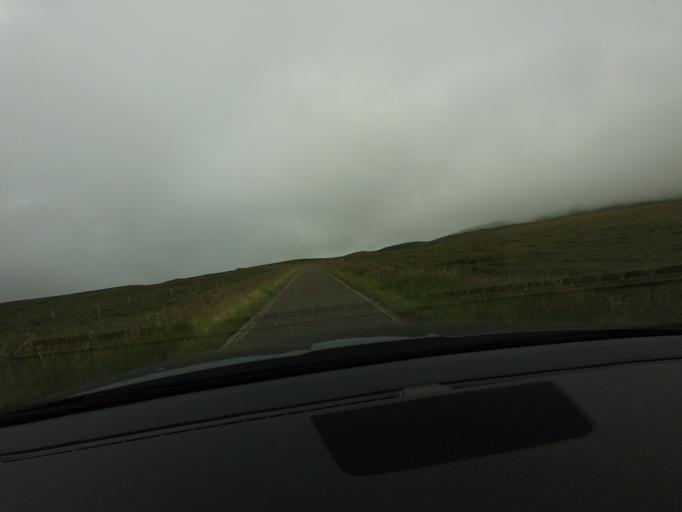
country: GB
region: Scotland
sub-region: Highland
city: Golspie
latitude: 58.4625
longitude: -4.3923
